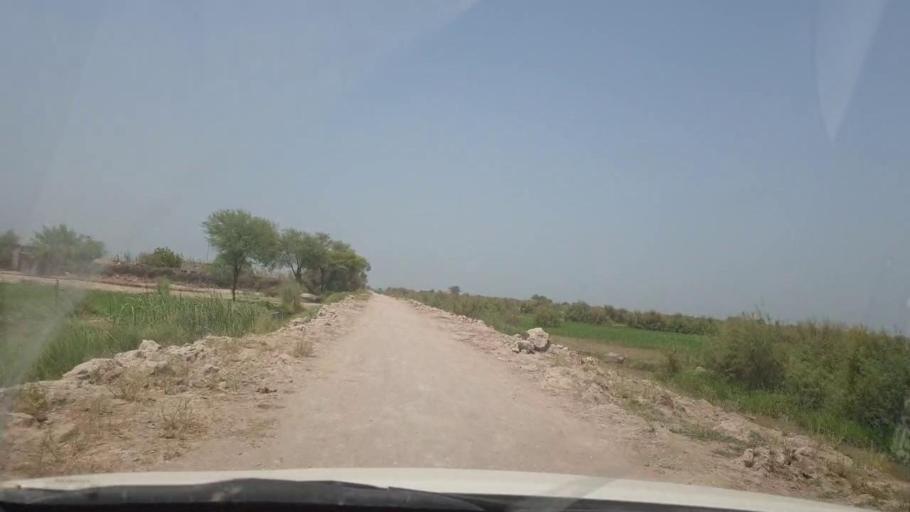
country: PK
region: Sindh
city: Lakhi
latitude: 27.8853
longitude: 68.7429
